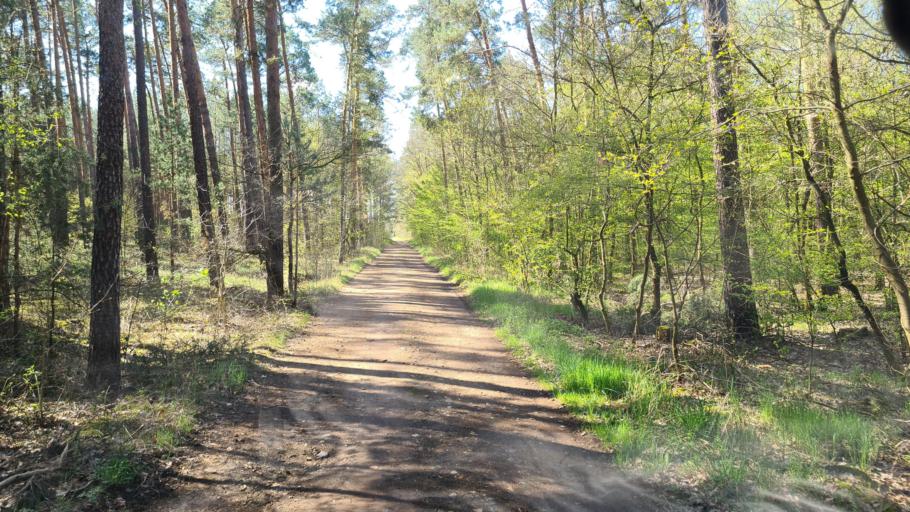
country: DE
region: Brandenburg
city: Altdobern
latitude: 51.6968
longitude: 14.0443
